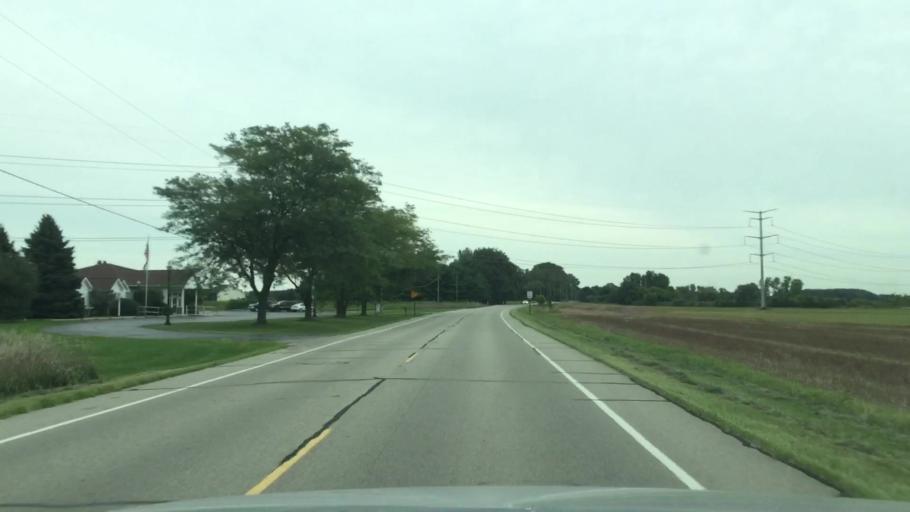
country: US
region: Michigan
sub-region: Washtenaw County
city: Milan
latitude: 42.1183
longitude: -83.7074
